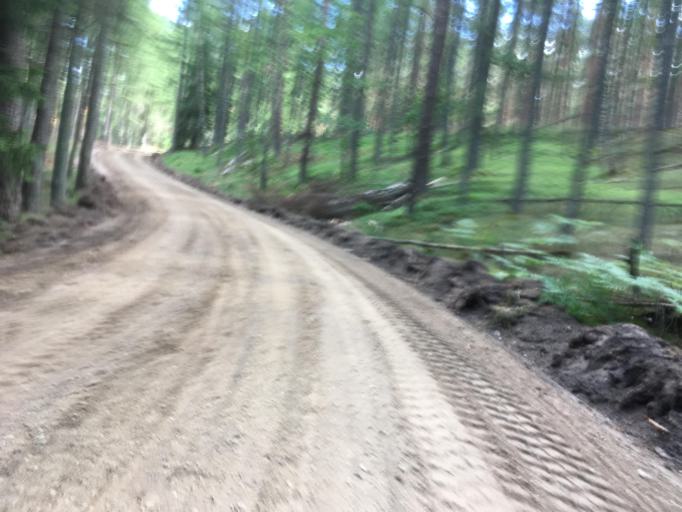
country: DE
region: Brandenburg
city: Joachimsthal
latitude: 52.9288
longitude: 13.7499
